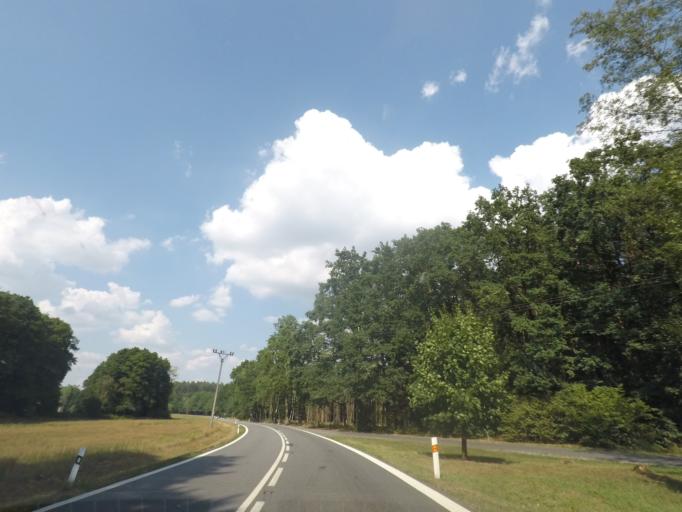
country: CZ
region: Pardubicky
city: Horni Jeleni
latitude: 50.0727
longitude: 16.0710
